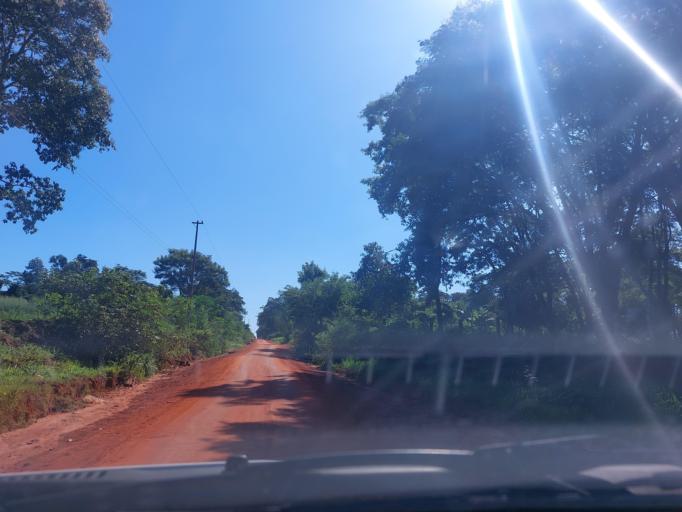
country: PY
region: San Pedro
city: Lima
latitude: -24.1699
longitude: -56.0134
